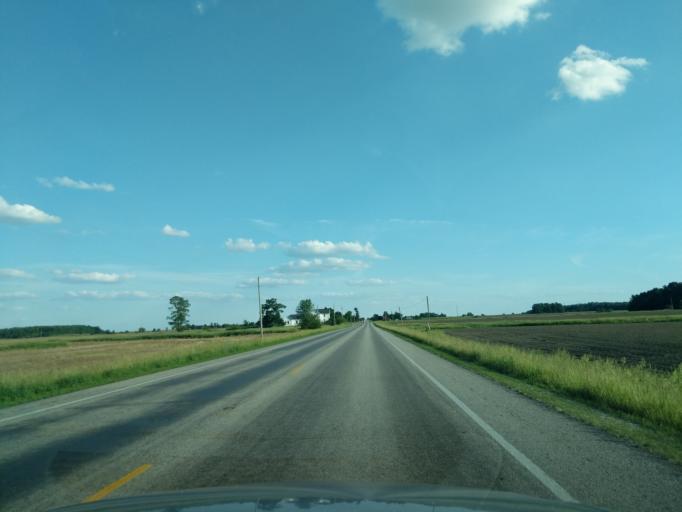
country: US
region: Indiana
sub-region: Huntington County
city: Roanoke
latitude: 40.9938
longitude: -85.4717
